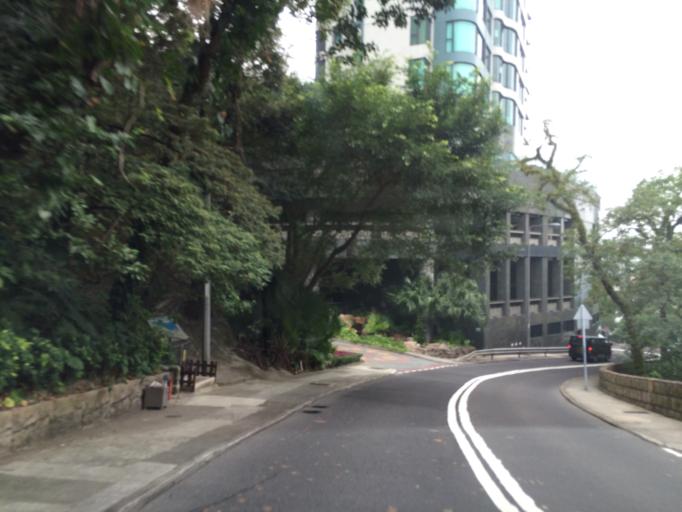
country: HK
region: Central and Western
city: Central
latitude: 22.2729
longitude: 114.1610
